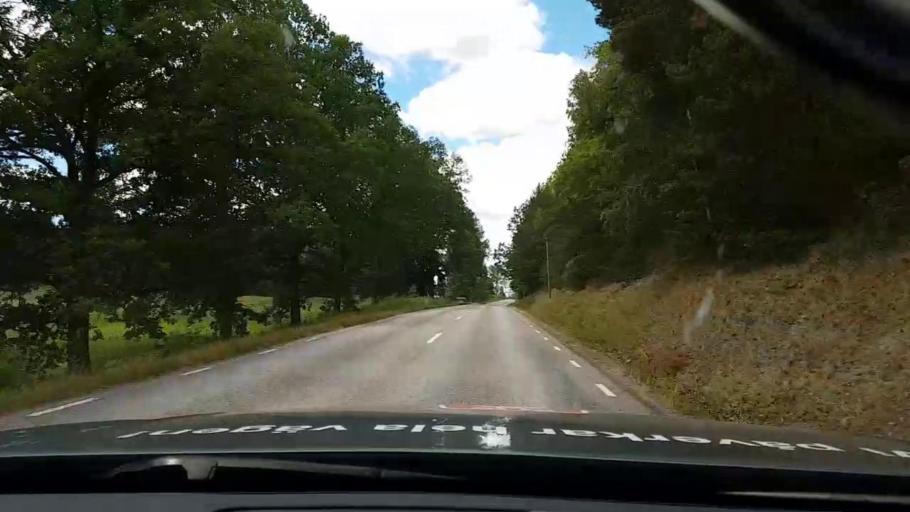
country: SE
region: Kalmar
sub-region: Vasterviks Kommun
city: Overum
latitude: 58.0759
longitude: 16.3615
